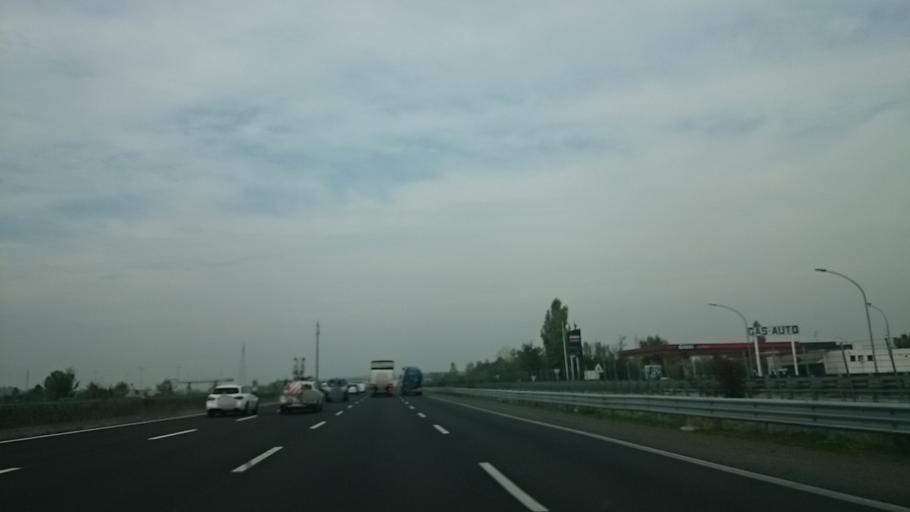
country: IT
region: Emilia-Romagna
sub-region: Provincia di Modena
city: Montale
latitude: 44.6068
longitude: 10.9126
